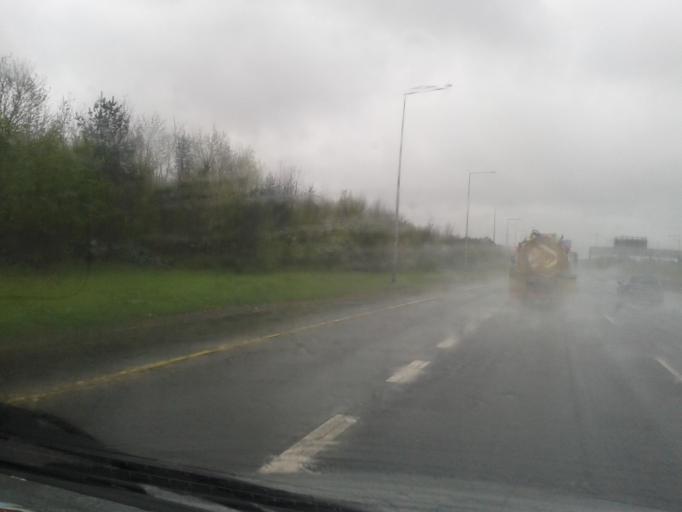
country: IE
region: Leinster
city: Ballymun
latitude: 53.4095
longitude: -6.2540
